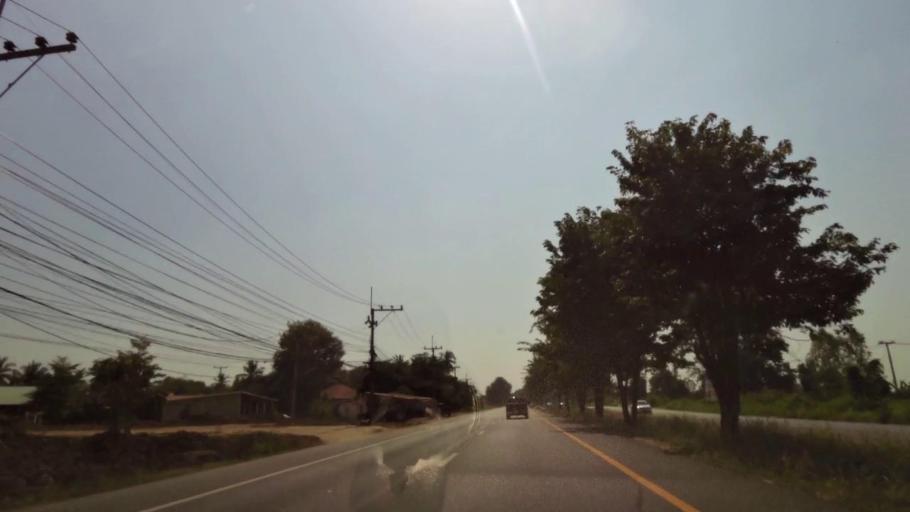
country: TH
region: Nakhon Sawan
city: Kao Liao
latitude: 15.9579
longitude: 100.1180
